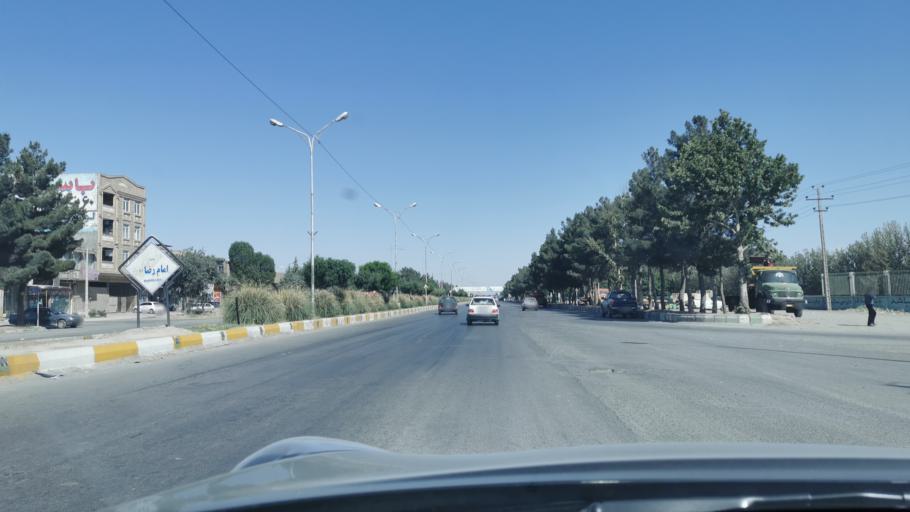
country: IR
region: Razavi Khorasan
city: Chenaran
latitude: 36.6355
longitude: 59.1279
